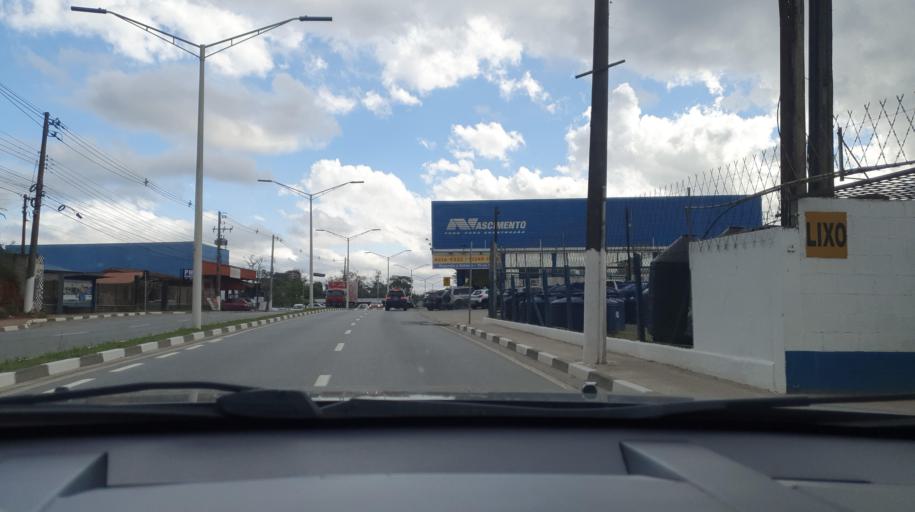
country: BR
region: Sao Paulo
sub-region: Vargem Grande Paulista
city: Vargem Grande Paulista
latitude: -23.6224
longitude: -46.9769
